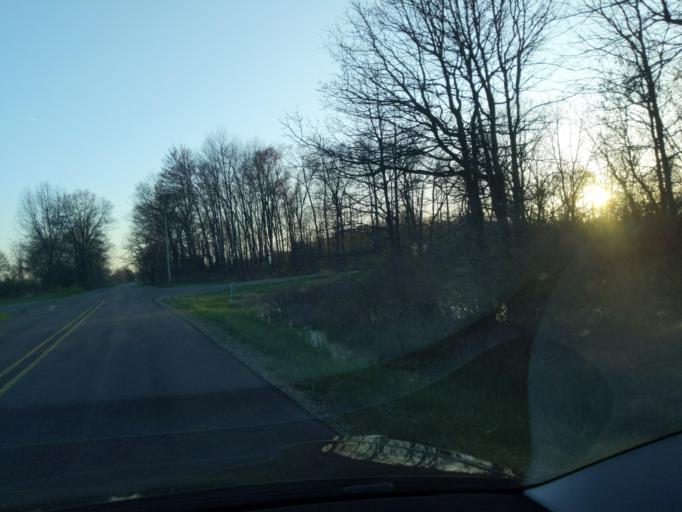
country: US
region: Michigan
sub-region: Ingham County
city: Stockbridge
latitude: 42.5025
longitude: -84.2665
